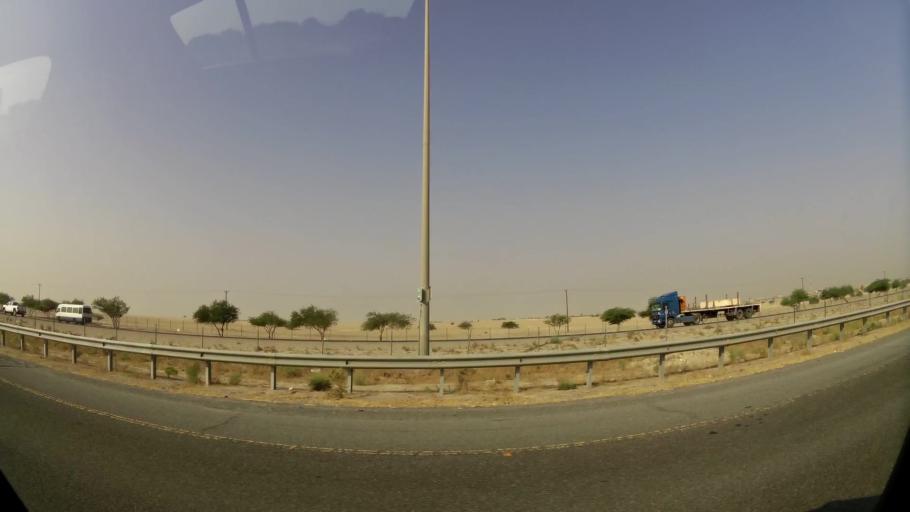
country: KW
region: Al Asimah
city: Ar Rabiyah
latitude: 29.2265
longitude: 47.8852
